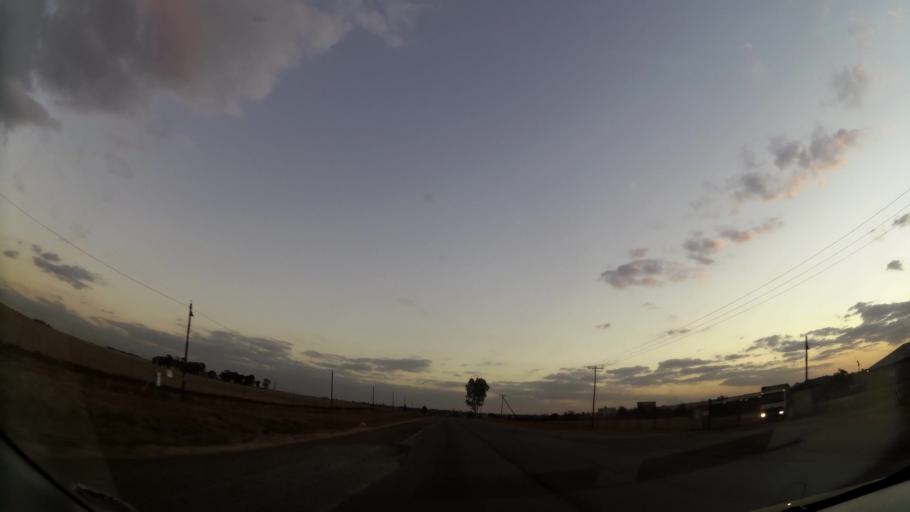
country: ZA
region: Gauteng
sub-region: West Rand District Municipality
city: Krugersdorp
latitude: -26.0550
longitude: 27.7073
